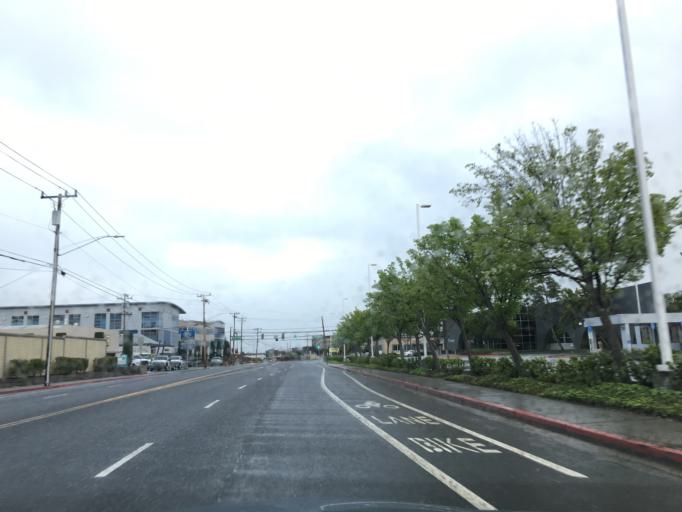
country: US
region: California
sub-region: San Mateo County
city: Belmont
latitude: 37.5203
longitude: -122.2662
